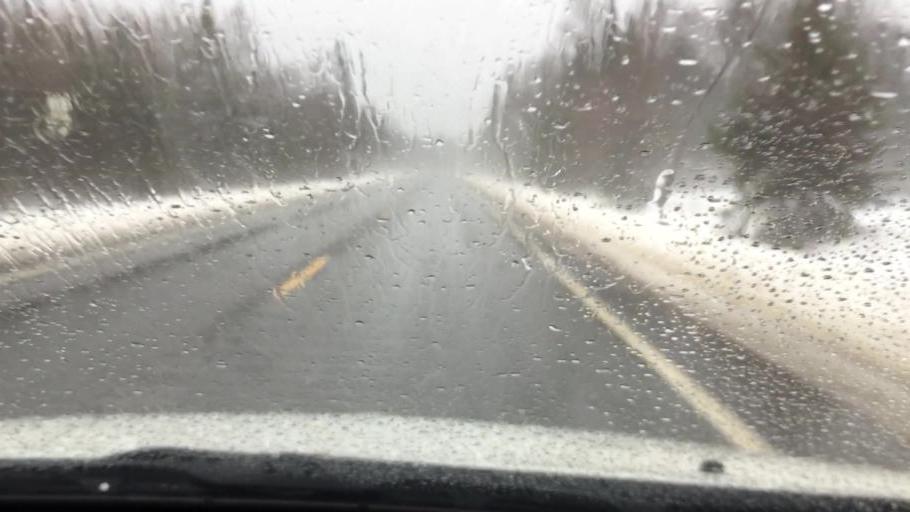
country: US
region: Michigan
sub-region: Charlevoix County
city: East Jordan
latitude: 45.0585
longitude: -85.0760
